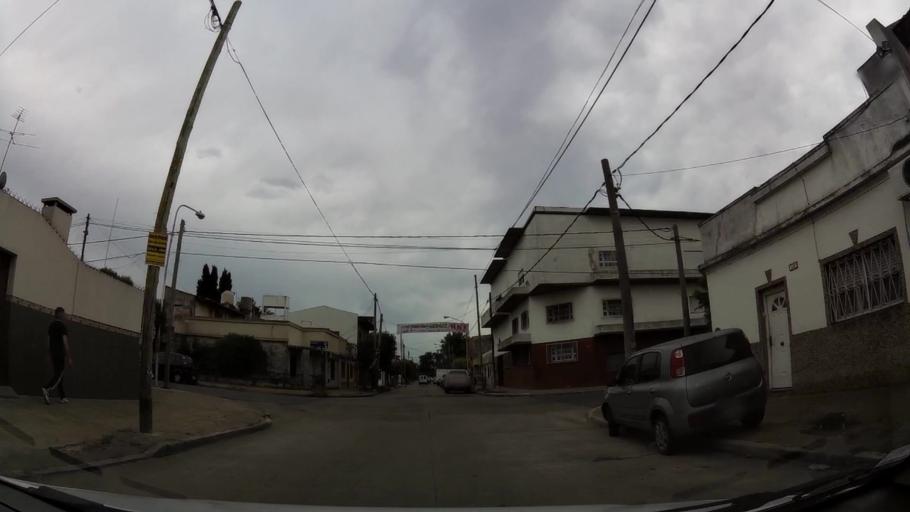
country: AR
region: Buenos Aires F.D.
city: Villa Lugano
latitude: -34.6687
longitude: -58.5119
